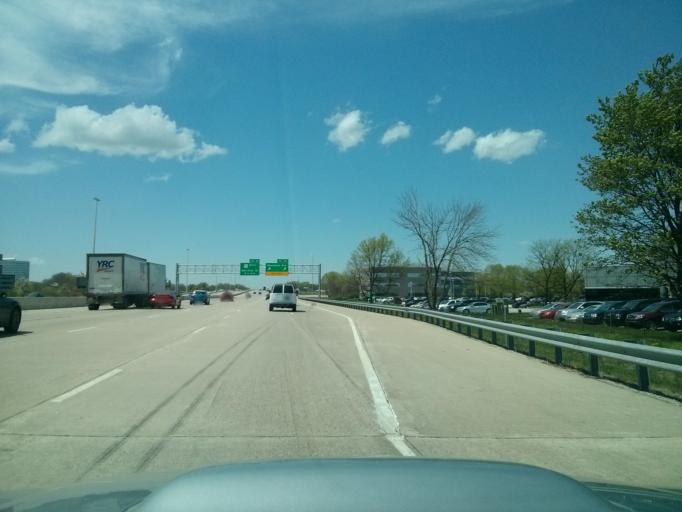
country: US
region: Indiana
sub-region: Marion County
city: Meridian Hills
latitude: 39.9192
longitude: -86.1042
